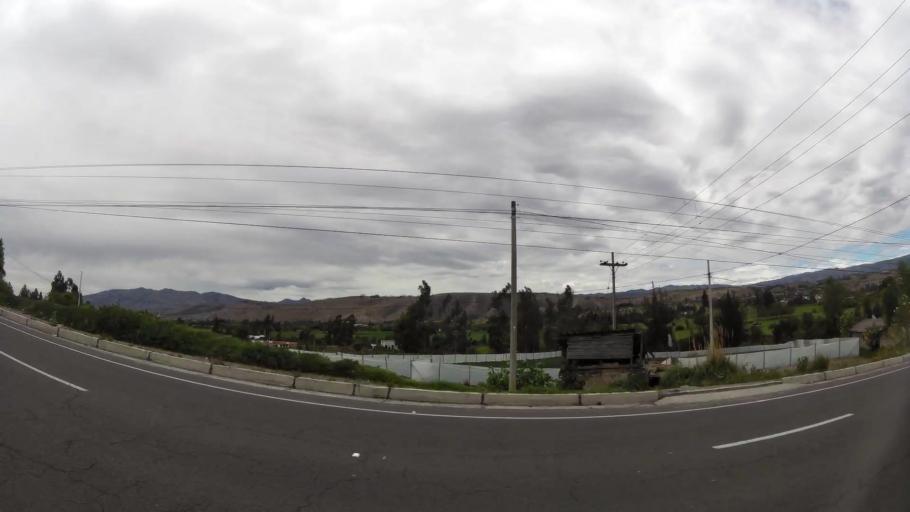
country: EC
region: Cotopaxi
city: Latacunga
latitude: -0.9843
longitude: -78.6018
